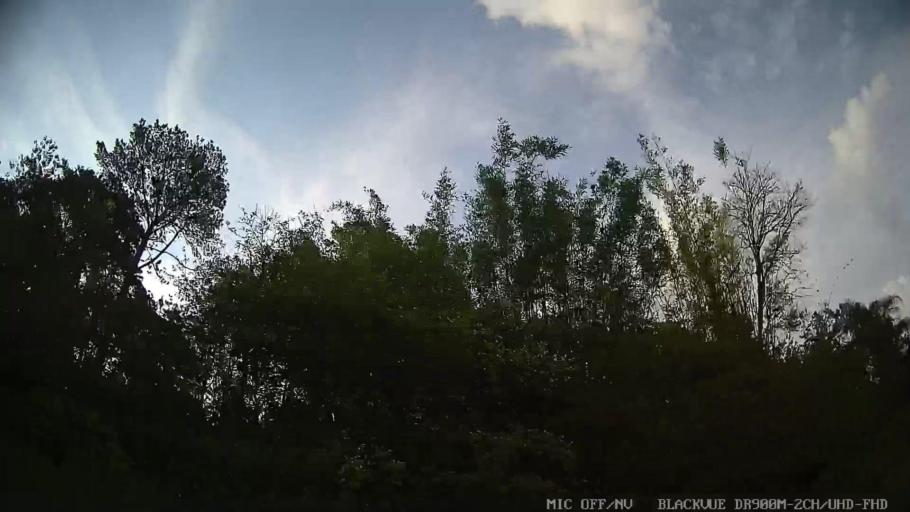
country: BR
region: Sao Paulo
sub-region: Braganca Paulista
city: Braganca Paulista
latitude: -22.9157
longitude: -46.4948
